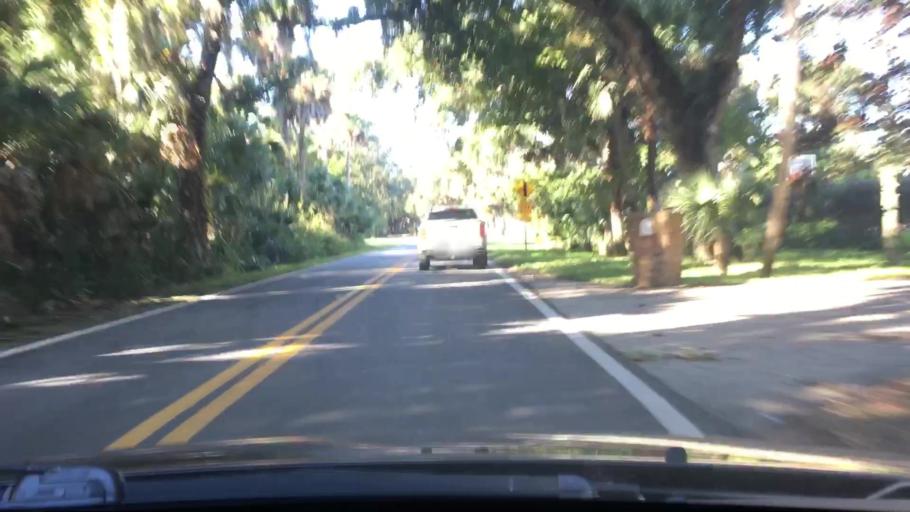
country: US
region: Florida
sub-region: Volusia County
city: Ormond-by-the-Sea
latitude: 29.3460
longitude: -81.0942
